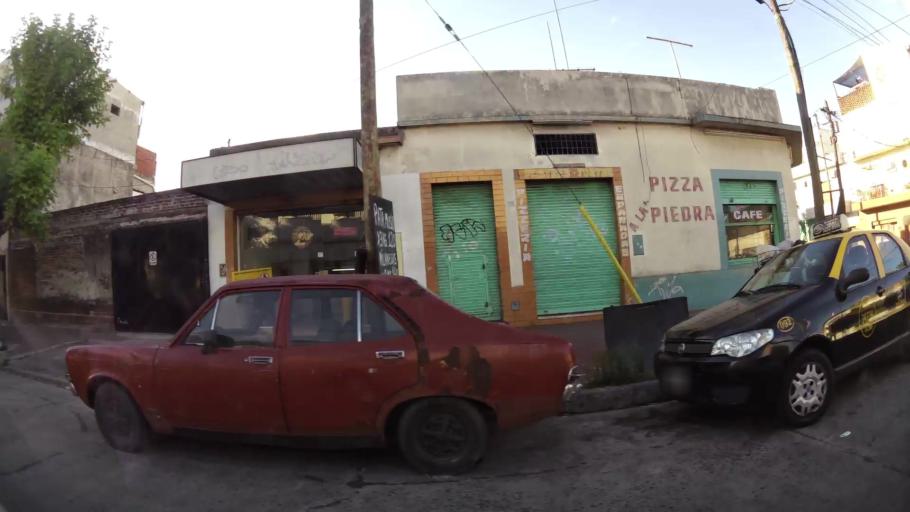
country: AR
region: Buenos Aires
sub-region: Partido de General San Martin
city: General San Martin
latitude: -34.5574
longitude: -58.5423
